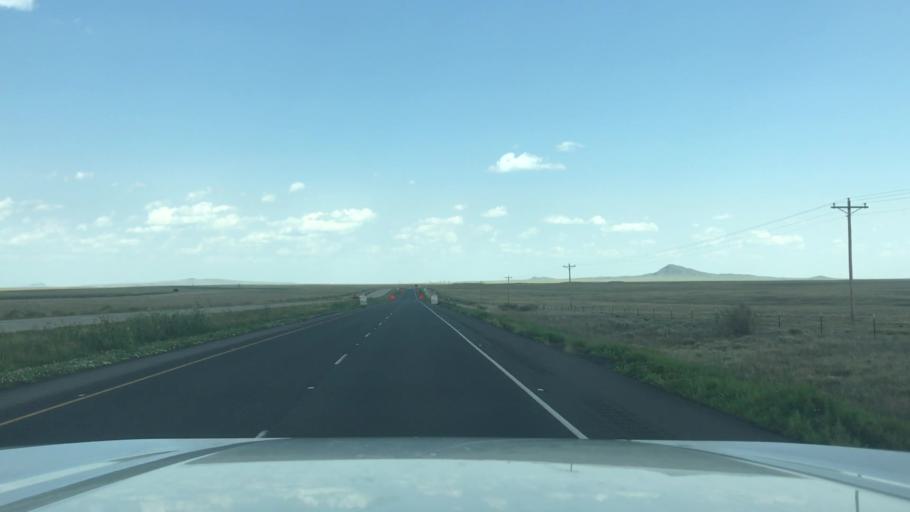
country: US
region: New Mexico
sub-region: Union County
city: Clayton
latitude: 36.6214
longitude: -103.6971
